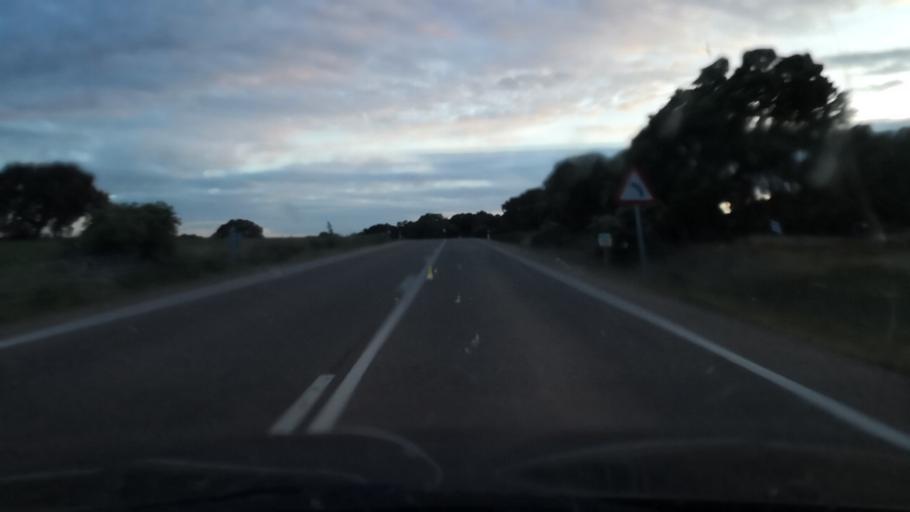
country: ES
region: Extremadura
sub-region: Provincia de Badajoz
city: Villar del Rey
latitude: 39.0474
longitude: -6.8042
